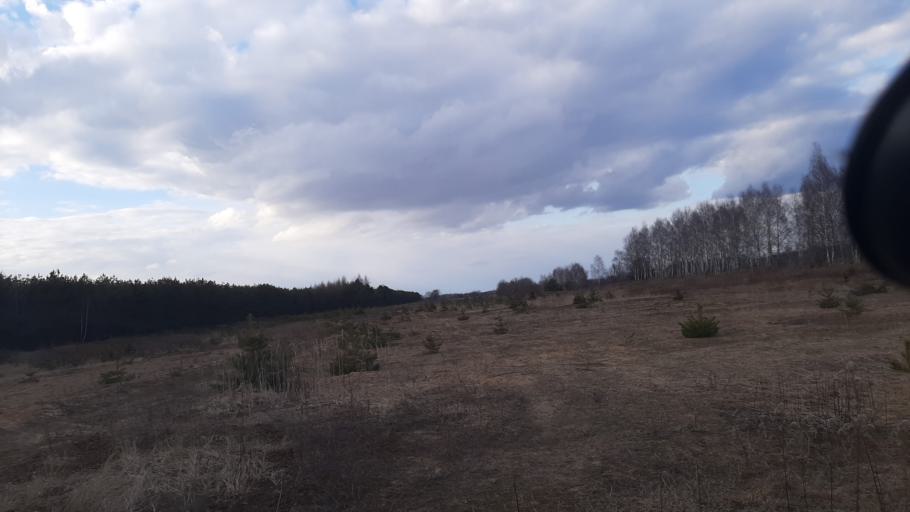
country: PL
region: Lublin Voivodeship
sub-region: Powiat lubelski
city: Jastkow
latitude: 51.3804
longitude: 22.4362
